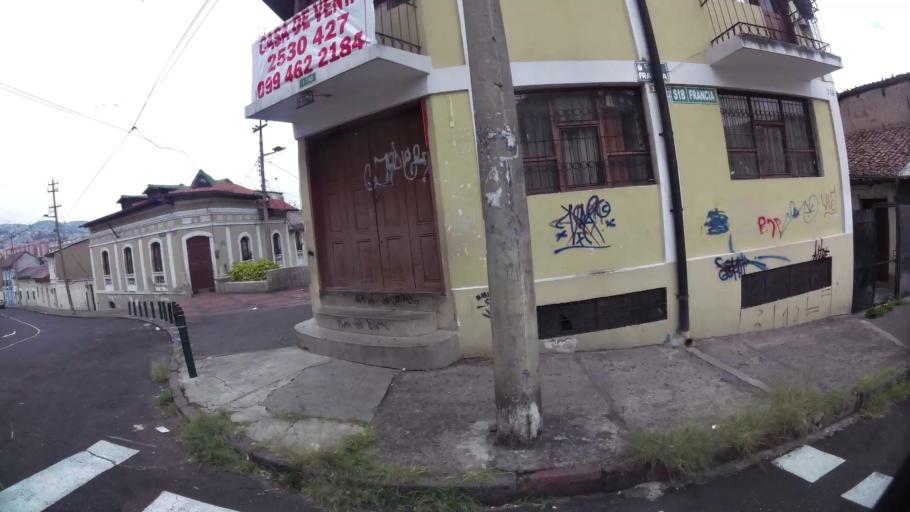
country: EC
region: Pichincha
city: Quito
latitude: -0.2286
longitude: -78.5101
